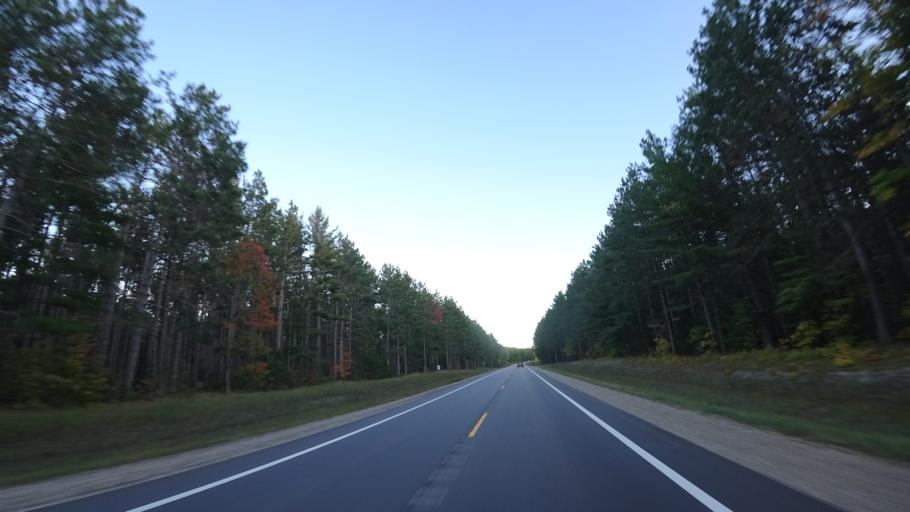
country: US
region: Michigan
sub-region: Luce County
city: Newberry
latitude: 46.3326
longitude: -85.0162
